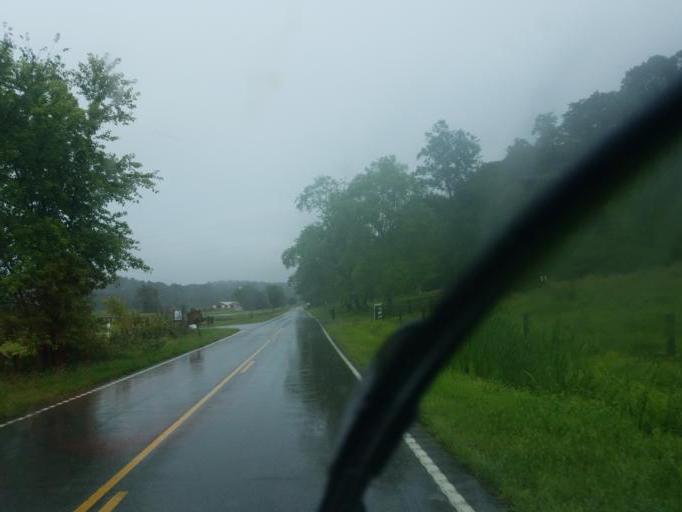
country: US
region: Ohio
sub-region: Scioto County
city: Franklin Furnace
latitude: 38.5975
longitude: -82.9468
